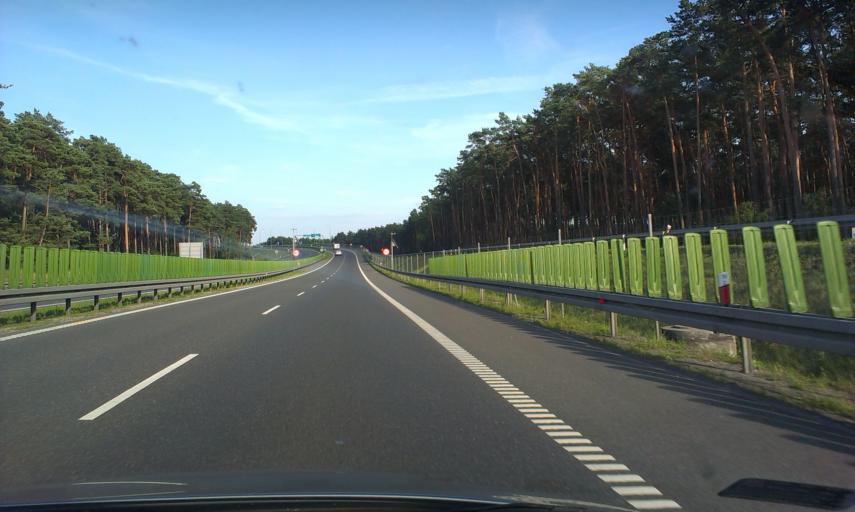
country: PL
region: Kujawsko-Pomorskie
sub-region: Bydgoszcz
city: Bydgoszcz
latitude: 53.0544
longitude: 17.9822
